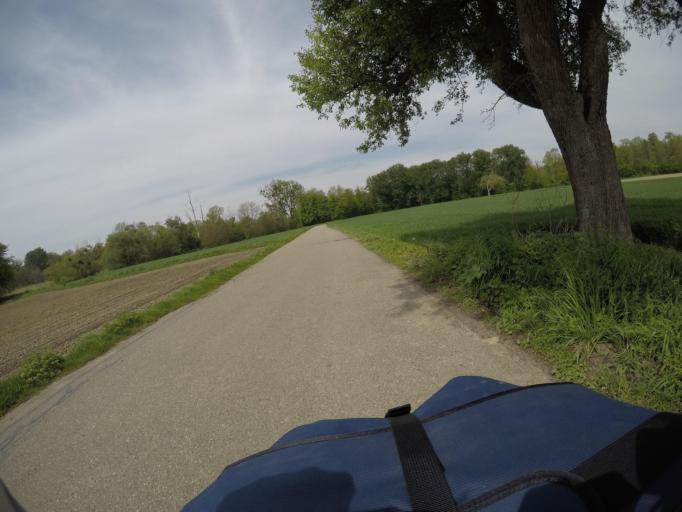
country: DE
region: Baden-Wuerttemberg
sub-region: Karlsruhe Region
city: Lichtenau
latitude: 48.7371
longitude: 7.9941
